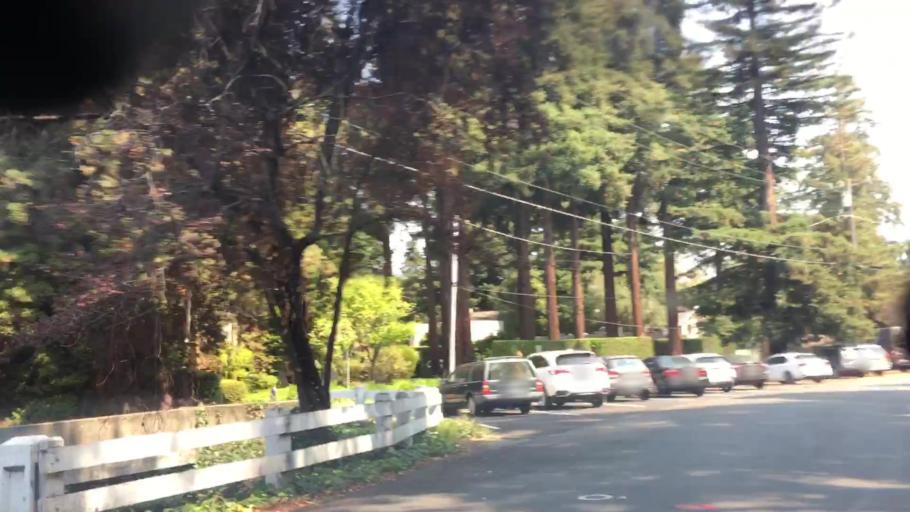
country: US
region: California
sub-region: Marin County
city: Mill Valley
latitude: 37.9034
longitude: -122.5442
